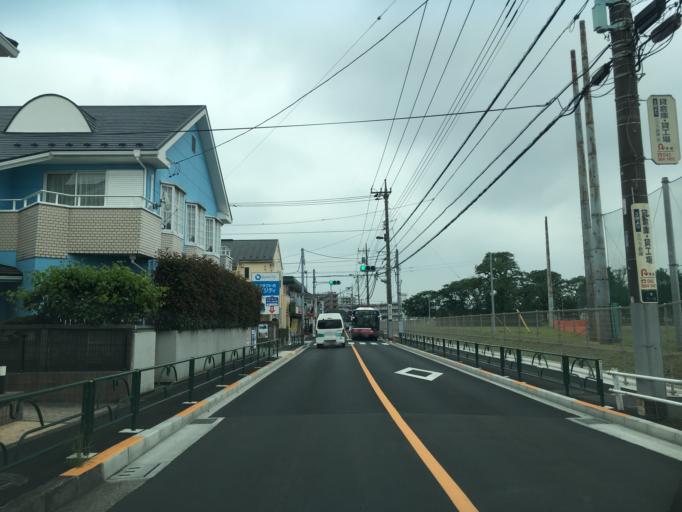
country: JP
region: Tokyo
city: Hino
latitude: 35.7360
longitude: 139.3958
